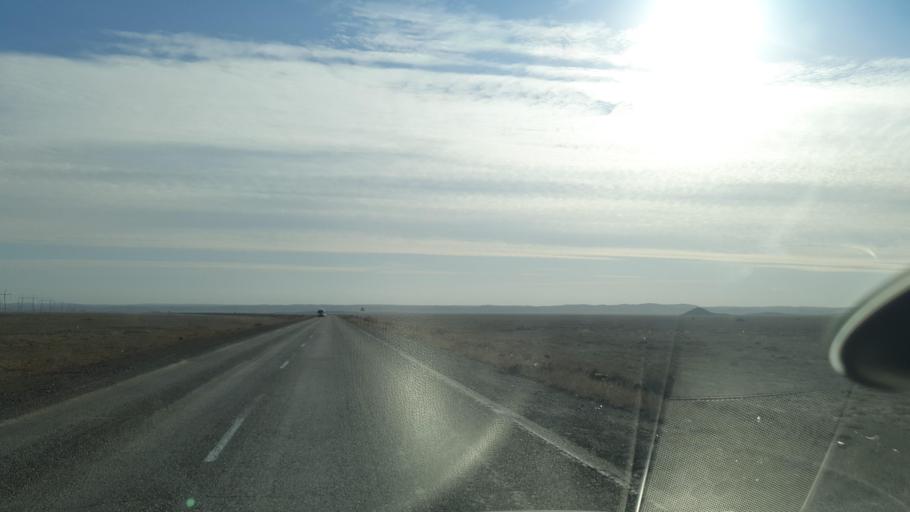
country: KZ
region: Zhambyl
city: Mynaral
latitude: 45.5960
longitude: 73.4000
